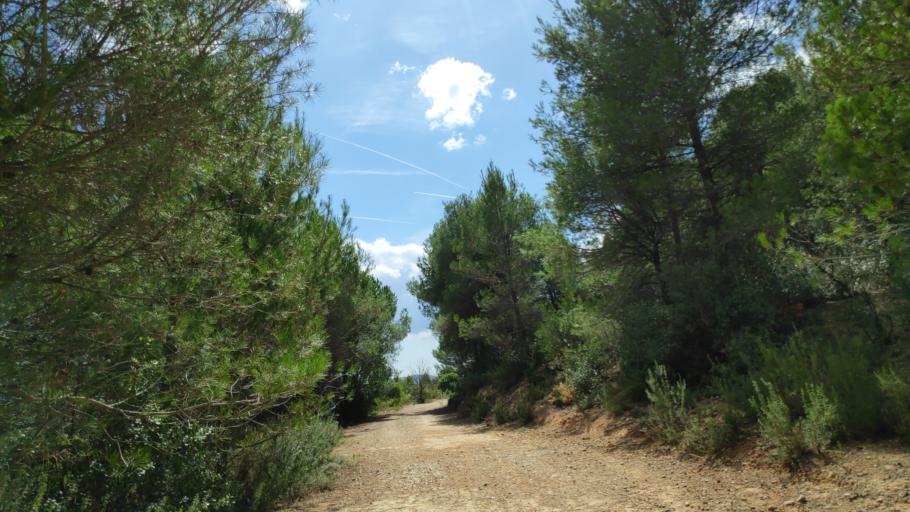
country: ES
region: Catalonia
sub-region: Provincia de Barcelona
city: Rubi
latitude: 41.5156
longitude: 2.0308
